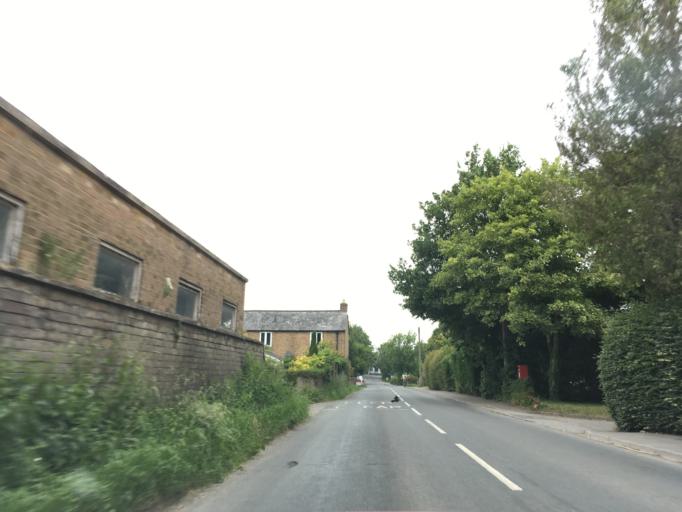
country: GB
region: England
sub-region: Gloucestershire
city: Stonehouse
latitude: 51.7732
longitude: -2.3660
